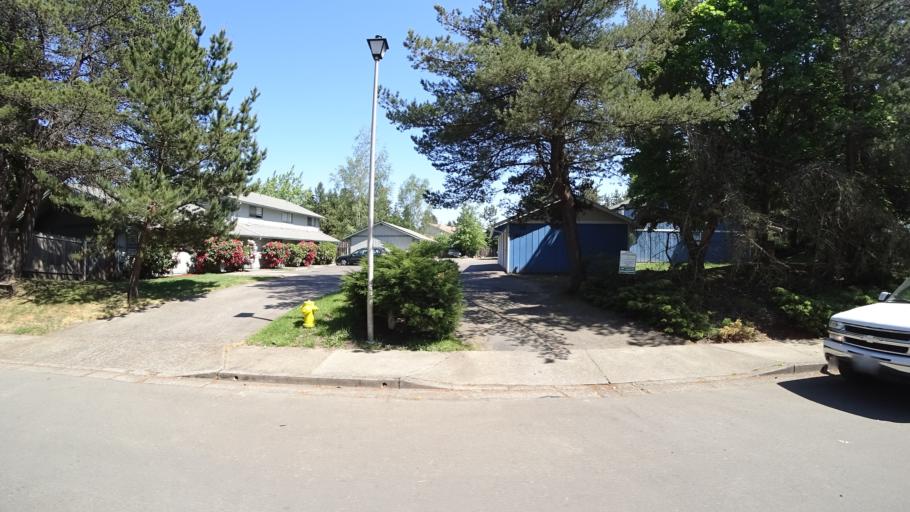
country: US
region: Oregon
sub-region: Washington County
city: Rockcreek
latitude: 45.5473
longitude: -122.8797
